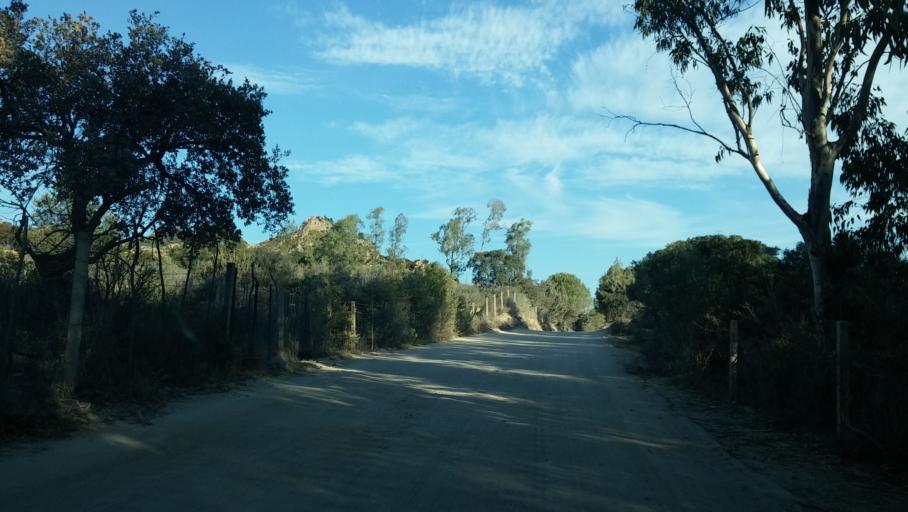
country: IT
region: Sardinia
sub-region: Provincia di Nuoro
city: La Caletta
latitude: 40.4840
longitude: 9.8021
